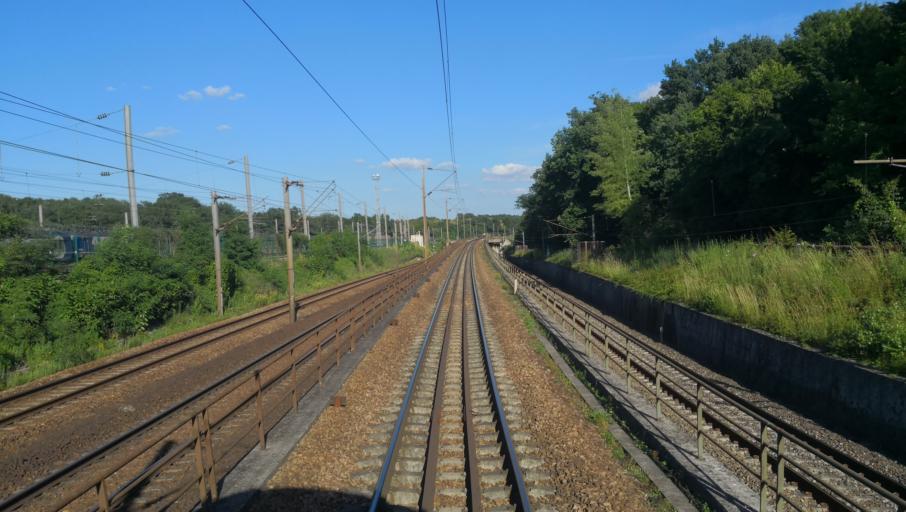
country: FR
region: Ile-de-France
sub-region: Departement des Yvelines
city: Le Mesnil-le-Roi
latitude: 48.9586
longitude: 2.1200
